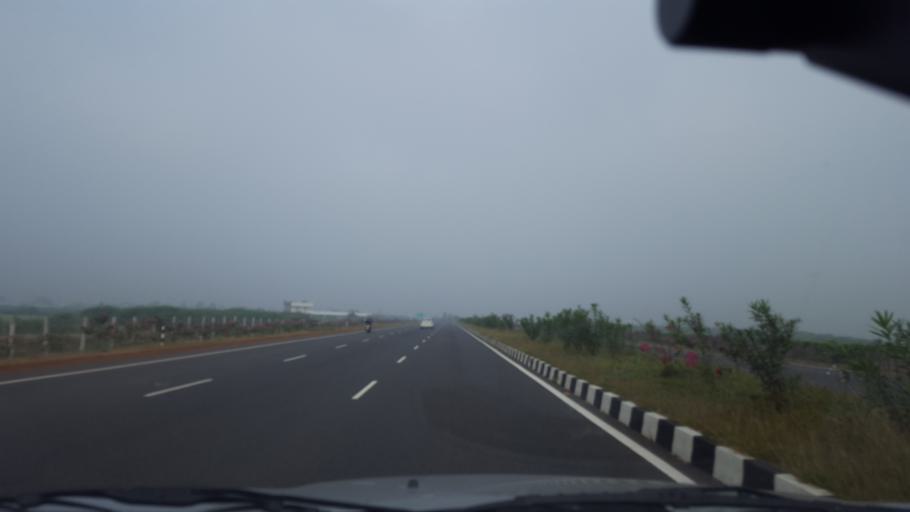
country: IN
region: Andhra Pradesh
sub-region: Prakasam
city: Ongole
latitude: 15.5244
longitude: 80.0612
